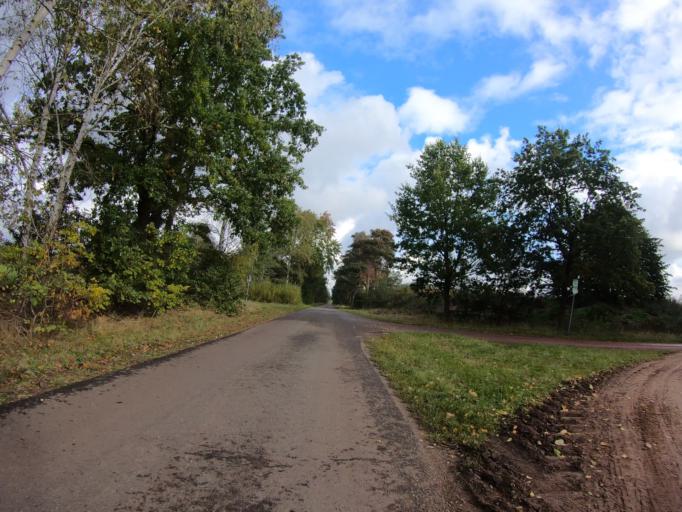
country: DE
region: Lower Saxony
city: Wahrenholz
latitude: 52.5859
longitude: 10.5762
